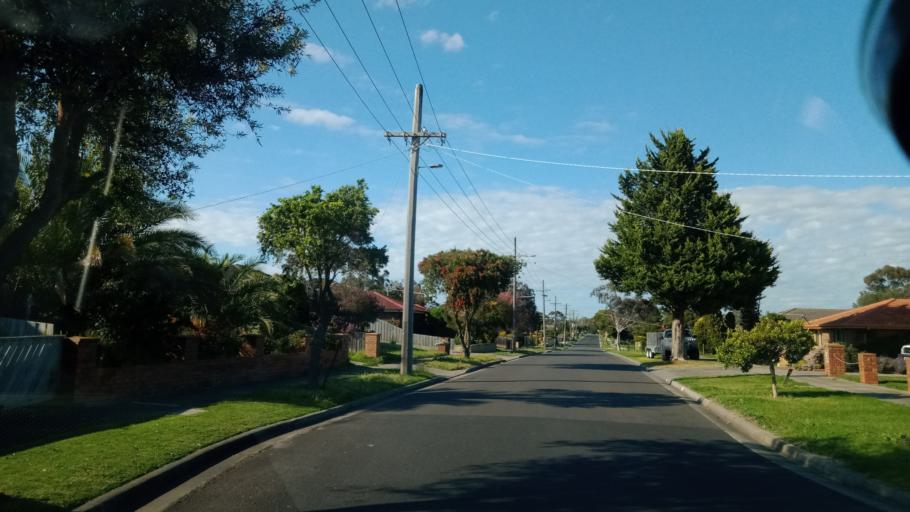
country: AU
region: Victoria
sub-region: Casey
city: Cranbourne West
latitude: -38.0928
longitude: 145.2717
